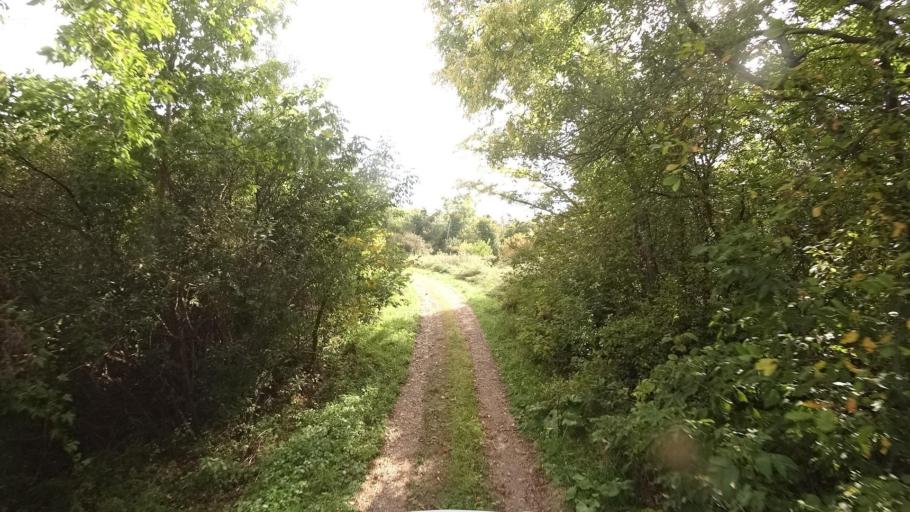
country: RU
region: Primorskiy
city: Dostoyevka
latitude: 44.3255
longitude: 133.4847
